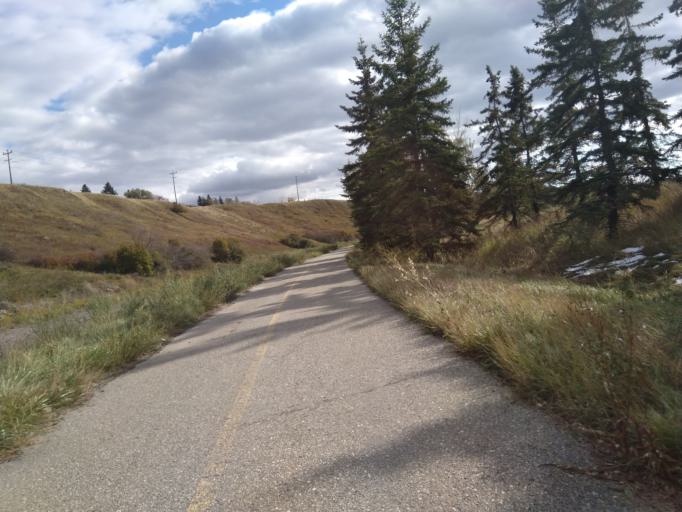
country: CA
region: Alberta
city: Calgary
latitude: 51.0337
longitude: -113.9973
